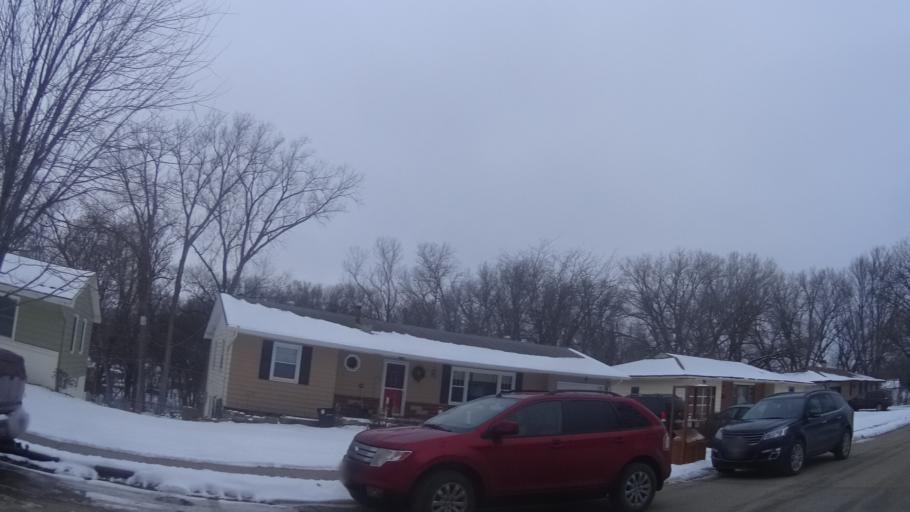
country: US
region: Nebraska
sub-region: Sarpy County
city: Offutt Air Force Base
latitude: 41.1365
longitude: -95.9206
